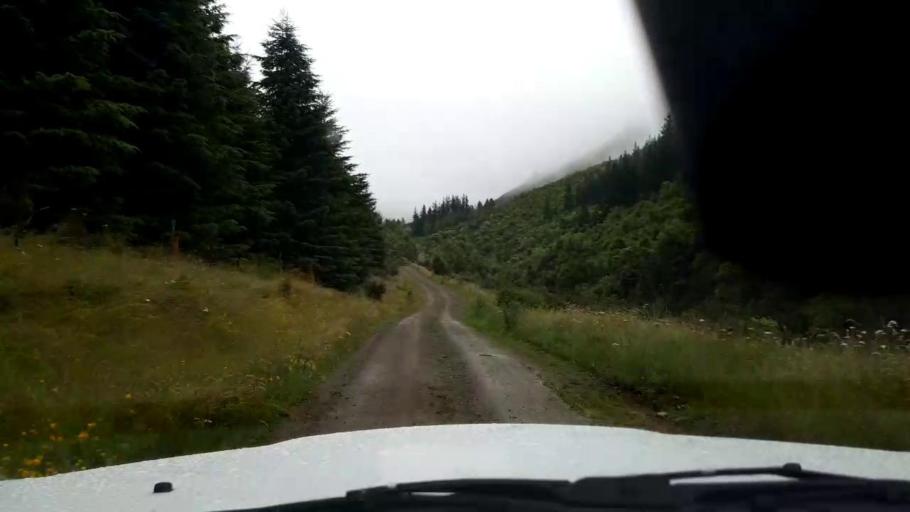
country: NZ
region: Canterbury
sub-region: Timaru District
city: Pleasant Point
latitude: -44.0391
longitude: 171.0149
